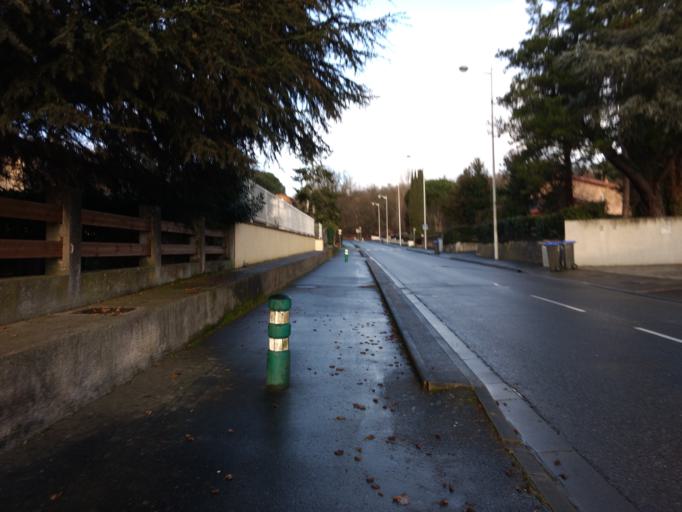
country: FR
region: Midi-Pyrenees
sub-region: Departement de la Haute-Garonne
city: Tournefeuille
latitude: 43.5915
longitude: 1.3394
